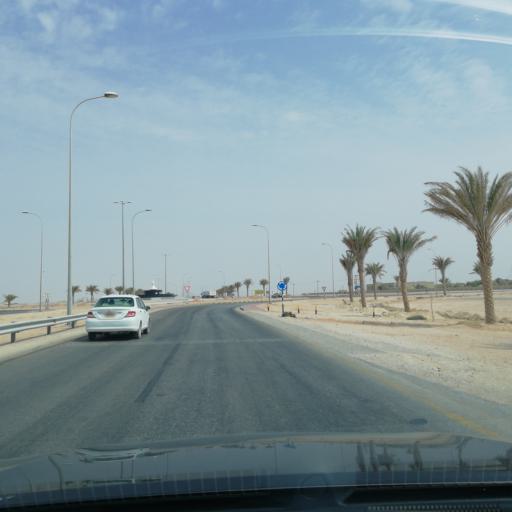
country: OM
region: Zufar
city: Salalah
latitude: 17.6113
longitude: 54.0331
